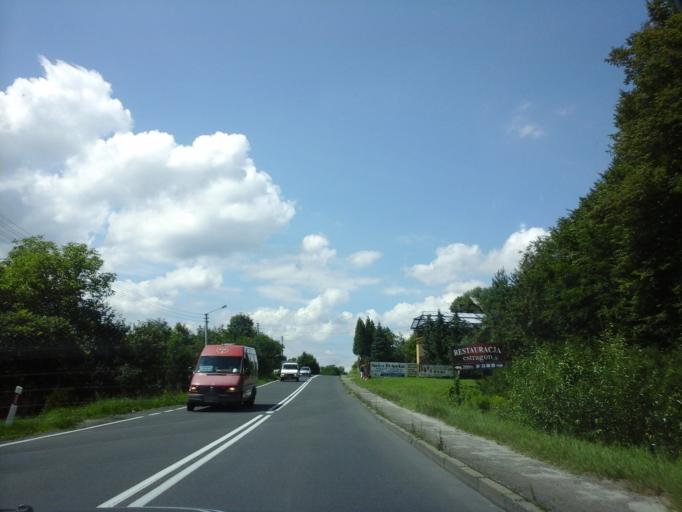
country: PL
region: Lesser Poland Voivodeship
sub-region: Powiat suski
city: Makow Podhalanski
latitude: 49.7327
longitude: 19.6559
